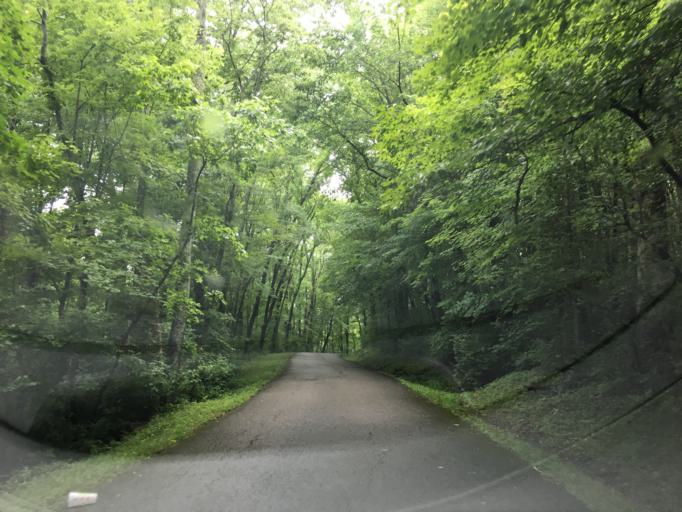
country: US
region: Tennessee
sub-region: Davidson County
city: Belle Meade
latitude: 36.0614
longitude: -86.9019
